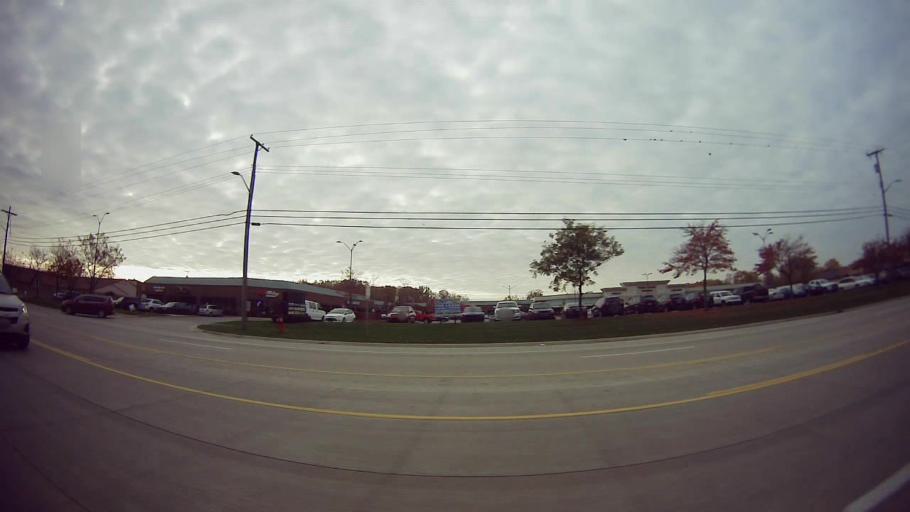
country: US
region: Michigan
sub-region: Oakland County
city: Clawson
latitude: 42.5339
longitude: -83.1246
